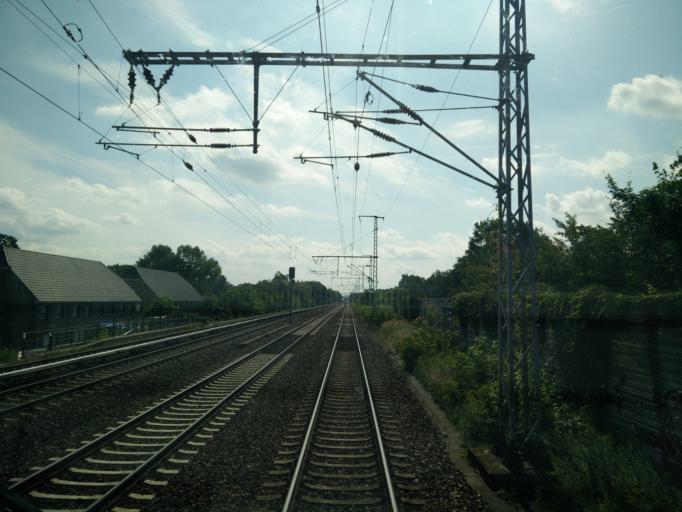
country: DE
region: Berlin
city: Karlshorst
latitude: 52.4764
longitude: 13.5361
